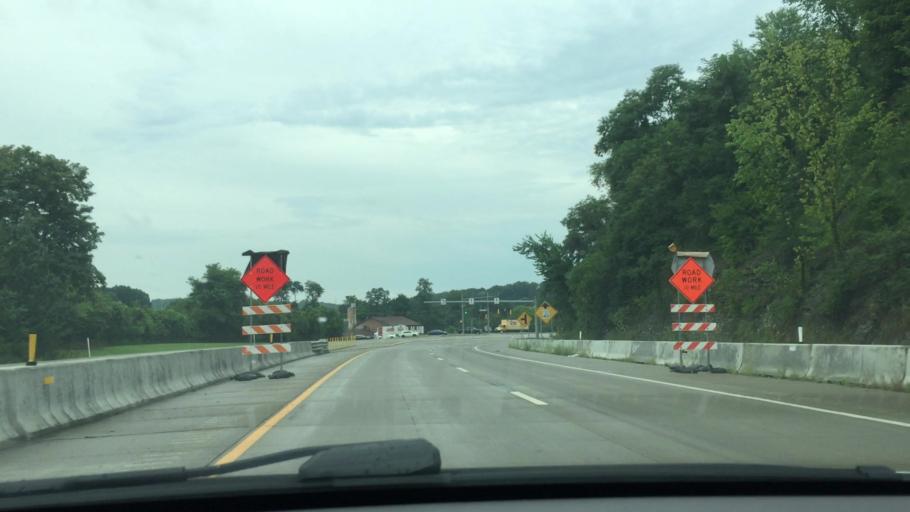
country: US
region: Pennsylvania
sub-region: Allegheny County
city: Bridgeville
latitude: 40.3565
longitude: -80.1280
